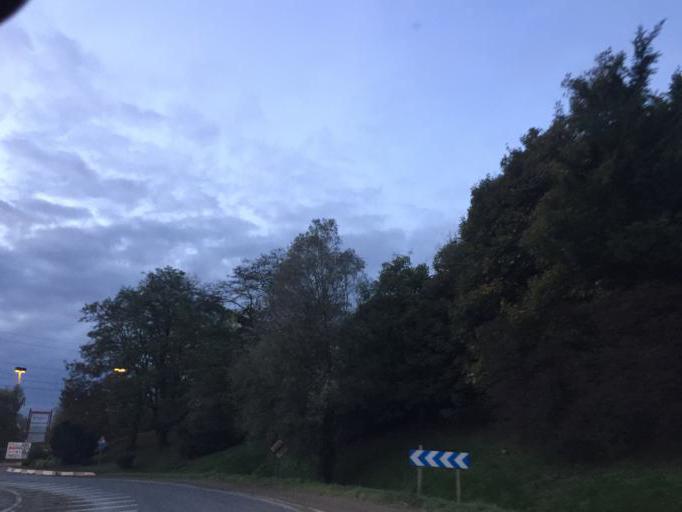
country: FR
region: Ile-de-France
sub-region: Departement de Seine-et-Marne
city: Annet-sur-Marne
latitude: 48.9478
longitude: 2.7217
